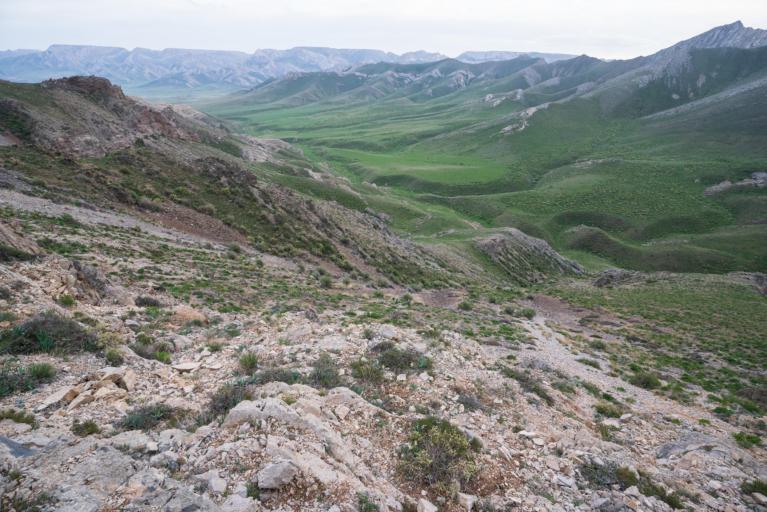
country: KZ
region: Ongtustik Qazaqstan
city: Ashchysay
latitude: 43.7575
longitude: 68.8119
